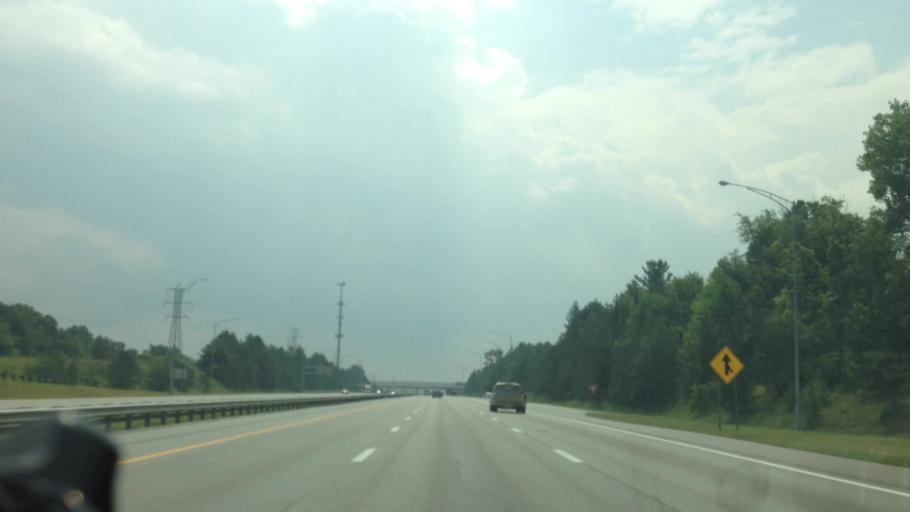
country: US
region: Ohio
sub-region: Cuyahoga County
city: Independence
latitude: 41.3425
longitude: -81.6500
